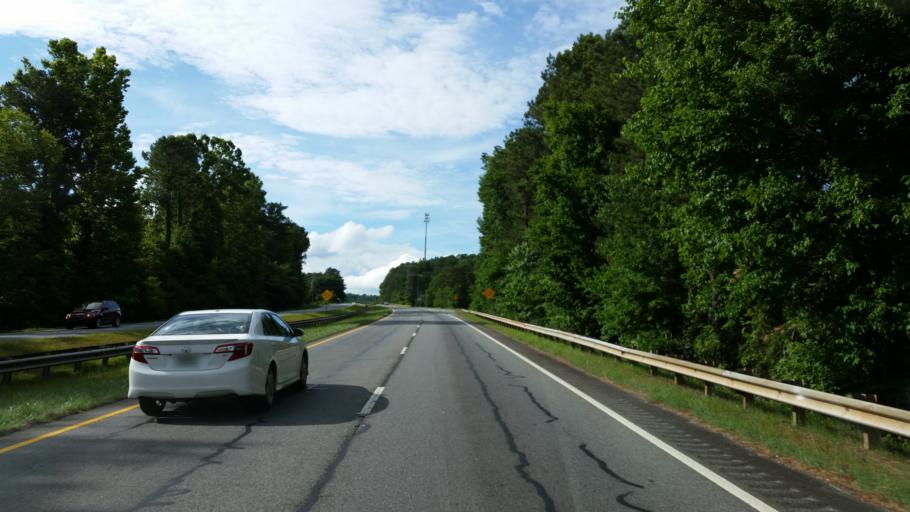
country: US
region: Georgia
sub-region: Bartow County
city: Emerson
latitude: 34.1189
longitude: -84.7491
